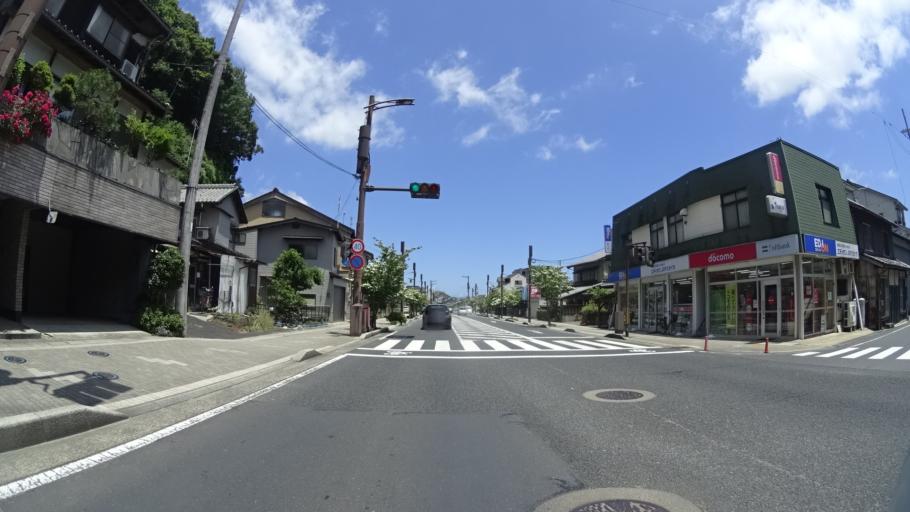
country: JP
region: Kyoto
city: Miyazu
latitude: 35.5311
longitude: 135.1921
